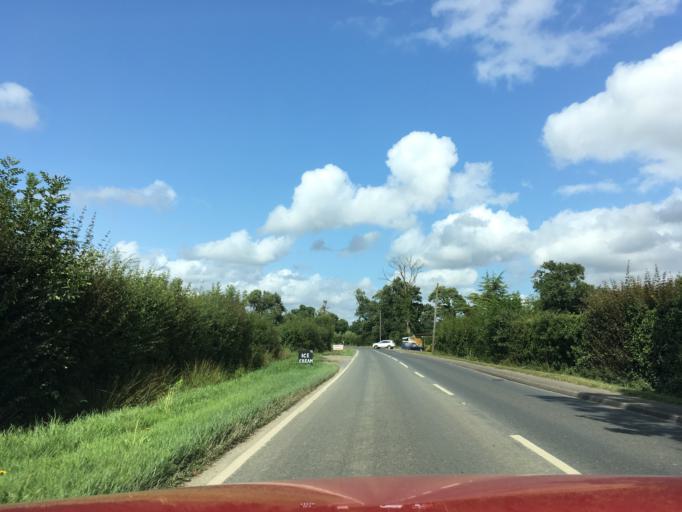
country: GB
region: England
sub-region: Kent
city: Headcorn
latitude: 51.1212
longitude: 0.6463
